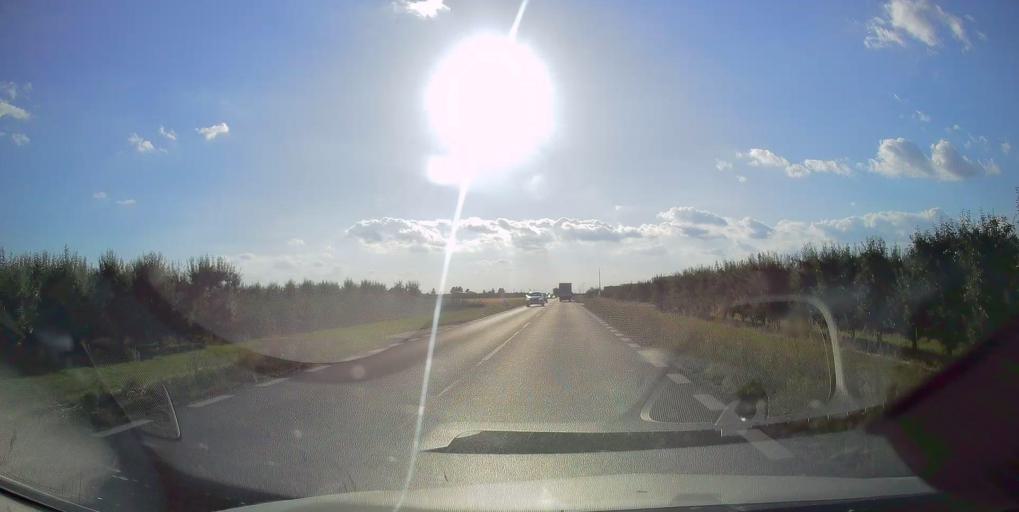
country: PL
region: Lodz Voivodeship
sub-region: Powiat rawski
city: Sadkowice
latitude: 51.8064
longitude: 20.5729
